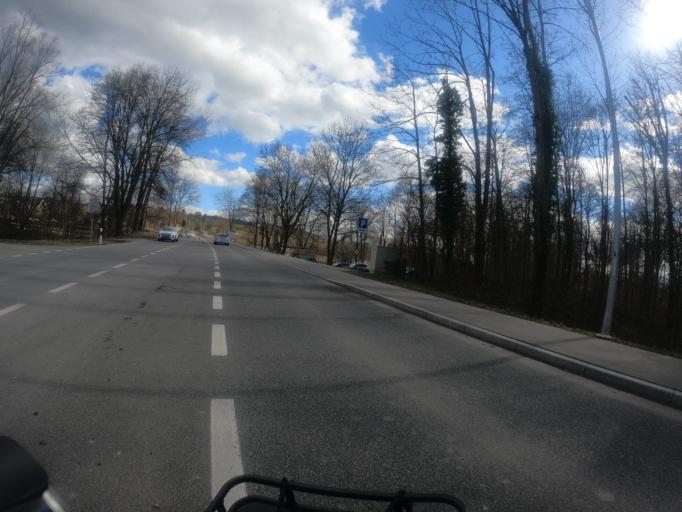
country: CH
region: Zurich
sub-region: Bezirk Affoltern
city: Ottenbach
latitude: 47.2793
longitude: 8.3927
